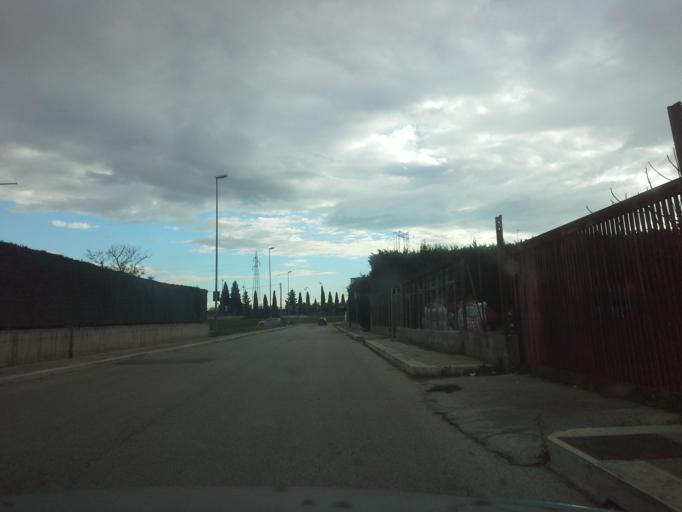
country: IT
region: Apulia
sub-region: Provincia di Bari
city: Adelfia
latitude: 41.0053
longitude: 16.8812
